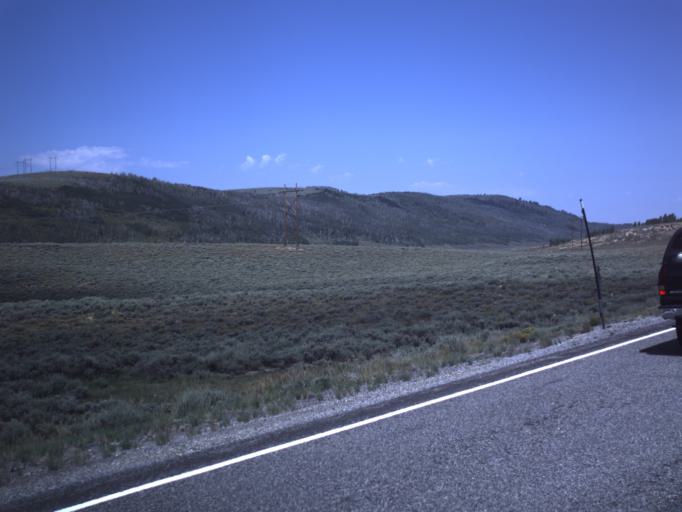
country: US
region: Utah
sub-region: Carbon County
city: Helper
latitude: 39.8418
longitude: -111.1289
